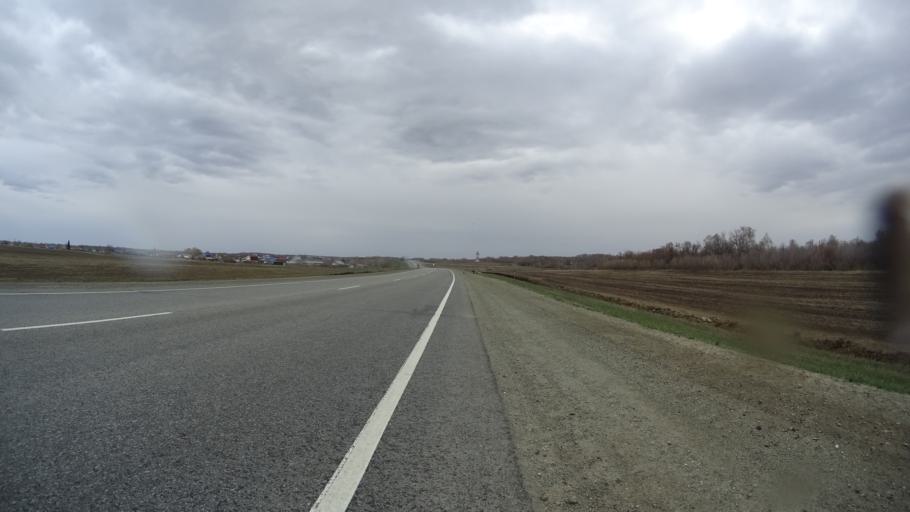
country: RU
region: Chelyabinsk
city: Krasnogorskiy
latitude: 54.6793
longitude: 61.2471
